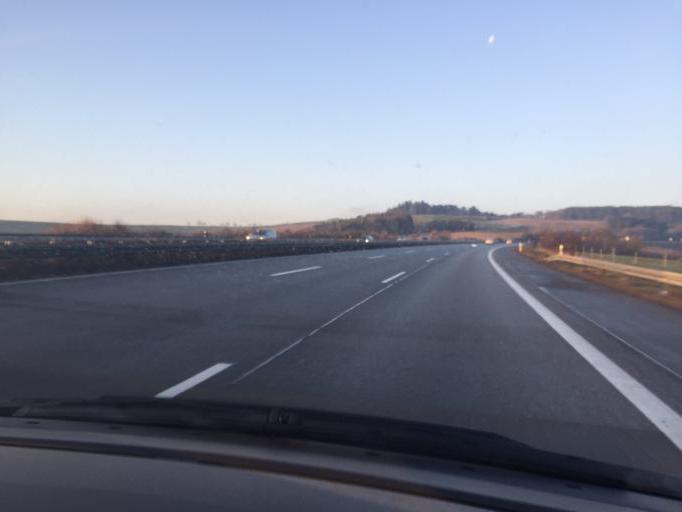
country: DE
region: Baden-Wuerttemberg
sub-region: Freiburg Region
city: Engen
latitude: 47.8881
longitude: 8.7439
